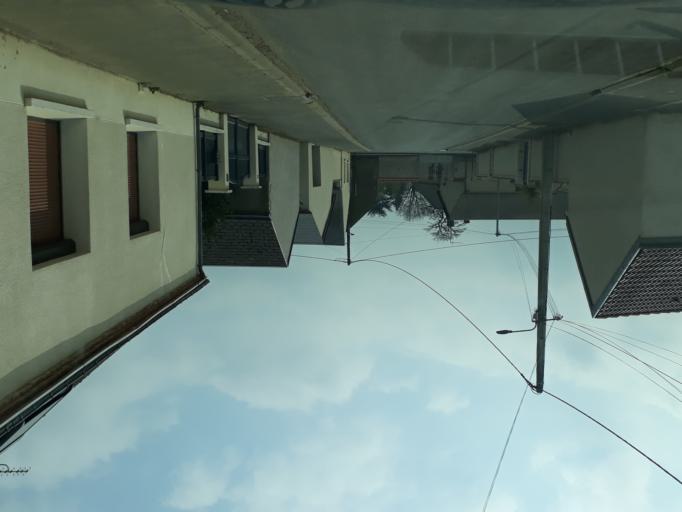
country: FR
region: Centre
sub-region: Departement du Loiret
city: Bricy
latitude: 48.0557
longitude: 1.7878
